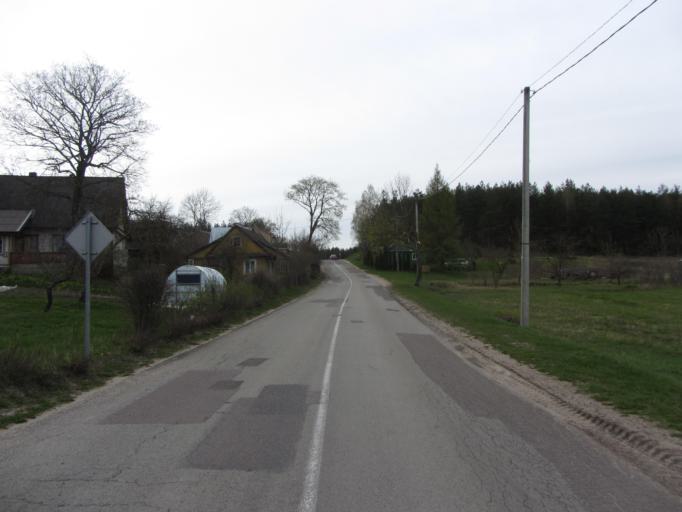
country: LT
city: Zarasai
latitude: 55.5835
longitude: 26.1293
